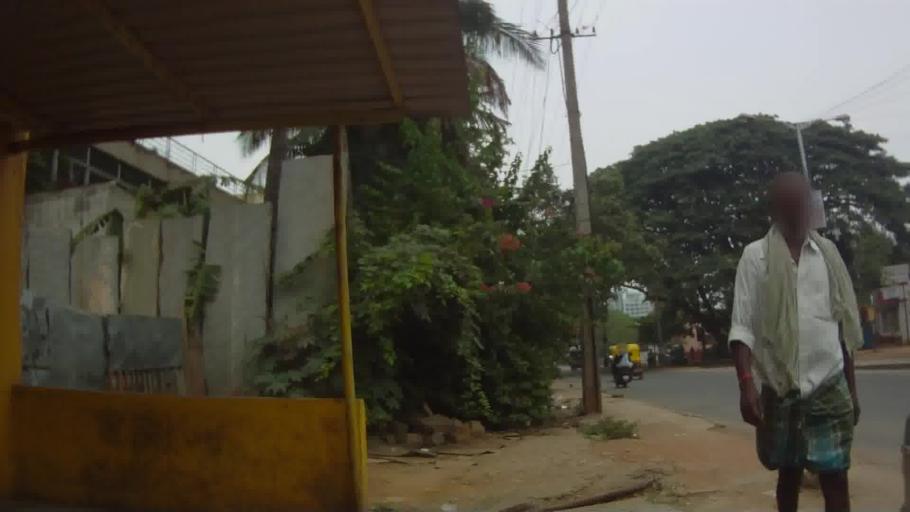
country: IN
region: Karnataka
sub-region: Bangalore Rural
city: Hoskote
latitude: 12.9561
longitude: 77.7291
